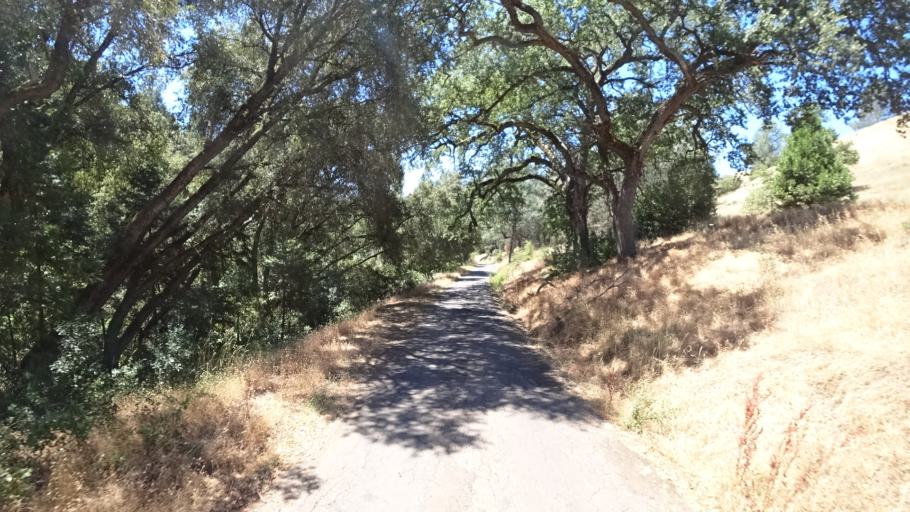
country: US
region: California
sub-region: Calaveras County
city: Forest Meadows
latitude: 38.1372
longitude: -120.4151
